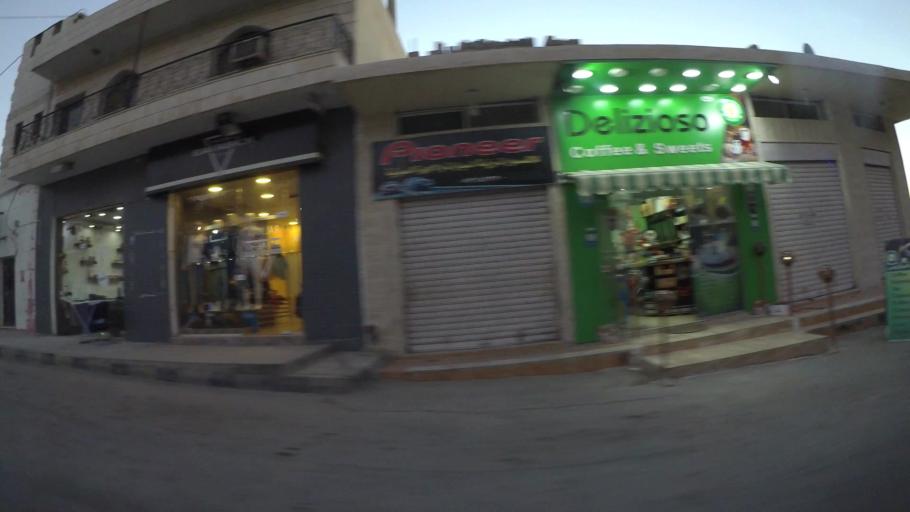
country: JO
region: Ma'an
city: Petra
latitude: 30.3202
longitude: 35.4812
